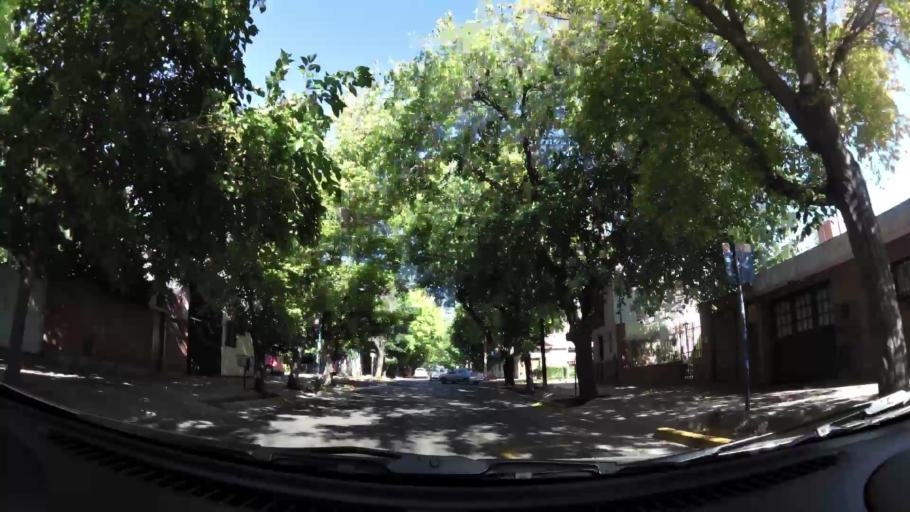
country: AR
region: Mendoza
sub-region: Departamento de Godoy Cruz
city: Godoy Cruz
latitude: -32.9239
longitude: -68.8567
